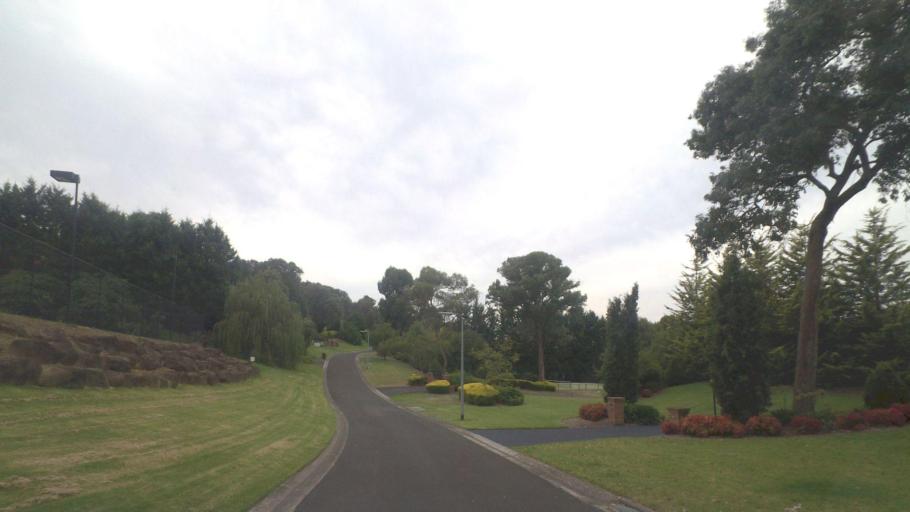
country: AU
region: Victoria
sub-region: Nillumbik
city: Eltham
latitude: -37.7451
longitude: 145.1816
